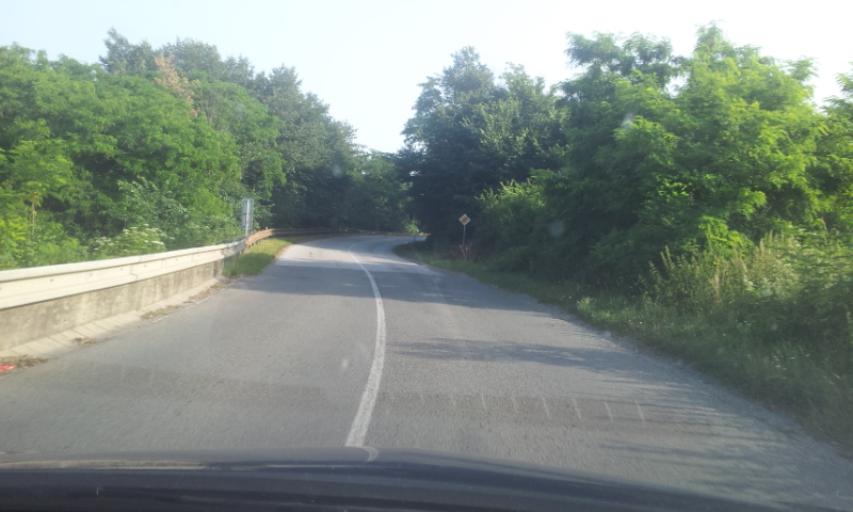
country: SK
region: Kosicky
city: Kosice
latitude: 48.6405
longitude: 21.3676
